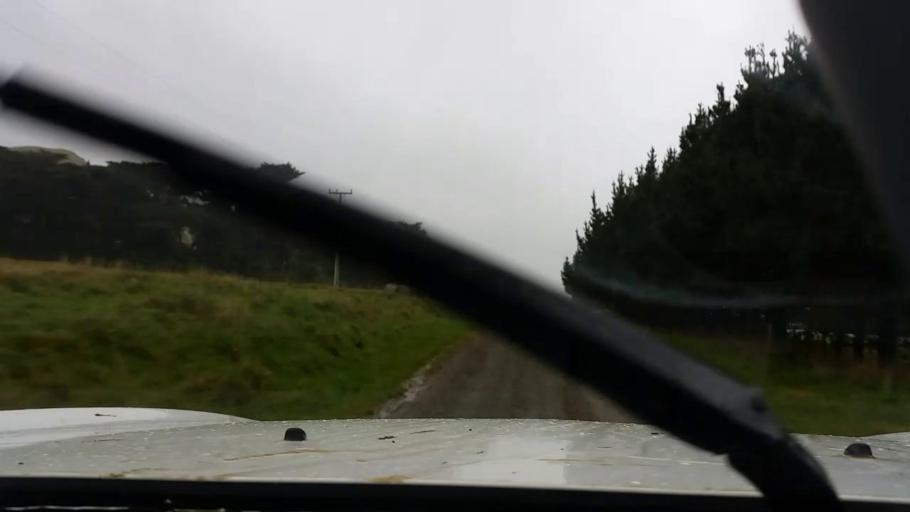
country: NZ
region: Wellington
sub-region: Masterton District
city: Masterton
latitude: -41.2583
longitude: 175.9016
